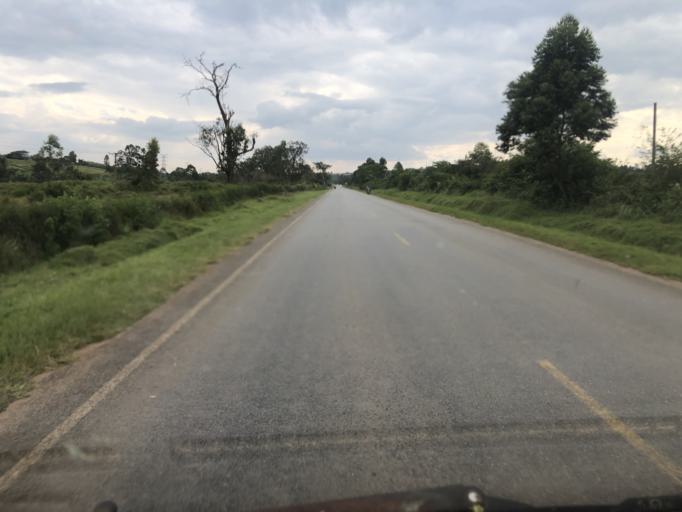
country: UG
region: Western Region
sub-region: Sheema District
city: Kibingo
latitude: -0.5799
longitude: 30.4304
